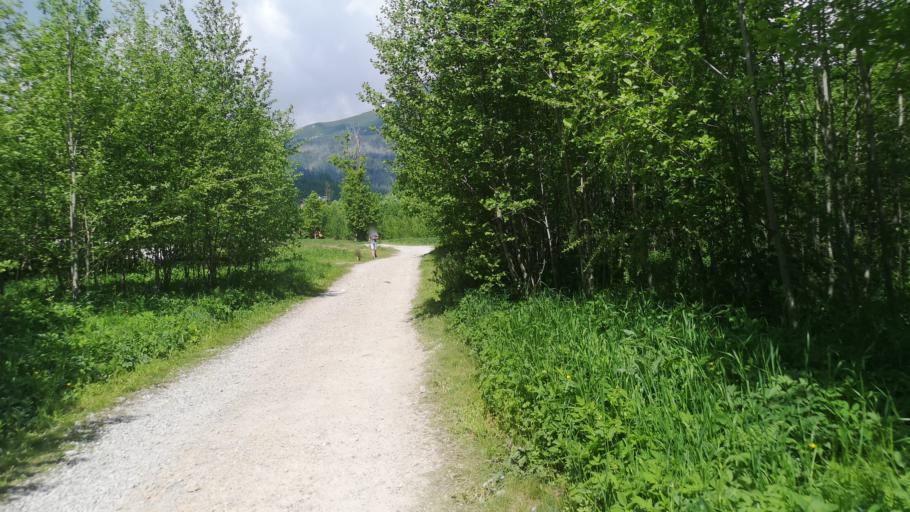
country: SK
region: Presovsky
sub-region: Okres Poprad
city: Vysoke Tatry
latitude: 49.1648
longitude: 20.2753
